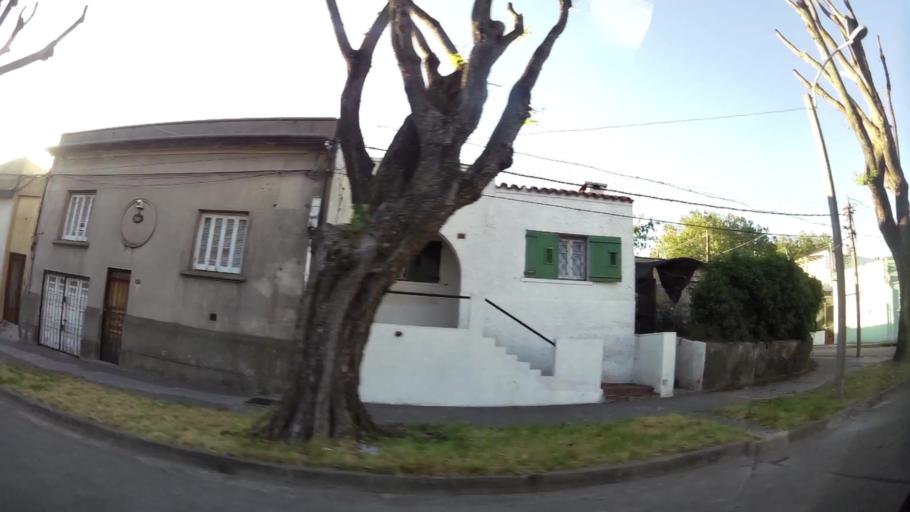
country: UY
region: Montevideo
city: Montevideo
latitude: -34.8497
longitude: -56.2049
